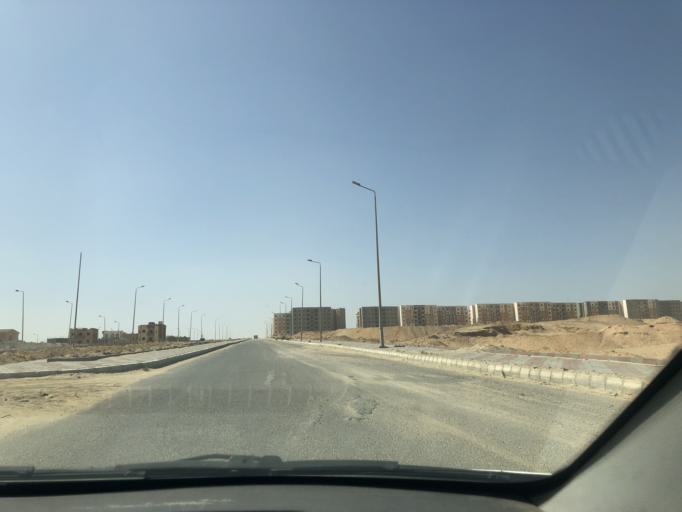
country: EG
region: Al Jizah
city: Madinat Sittah Uktubar
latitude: 29.9317
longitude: 31.0109
